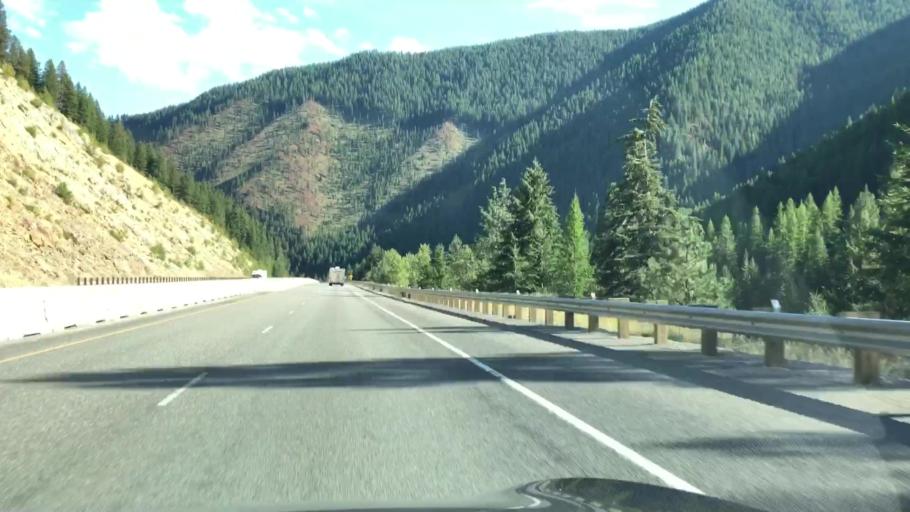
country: US
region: Montana
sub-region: Sanders County
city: Thompson Falls
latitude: 47.3077
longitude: -115.2070
